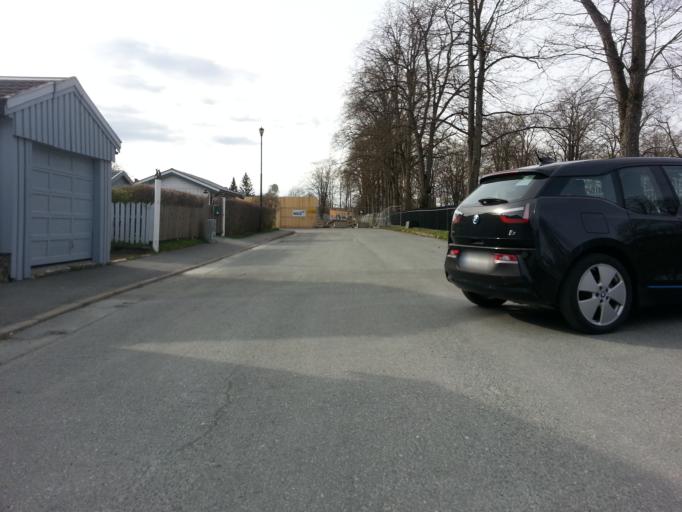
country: NO
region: Sor-Trondelag
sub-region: Trondheim
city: Trondheim
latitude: 63.4162
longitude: 10.3926
